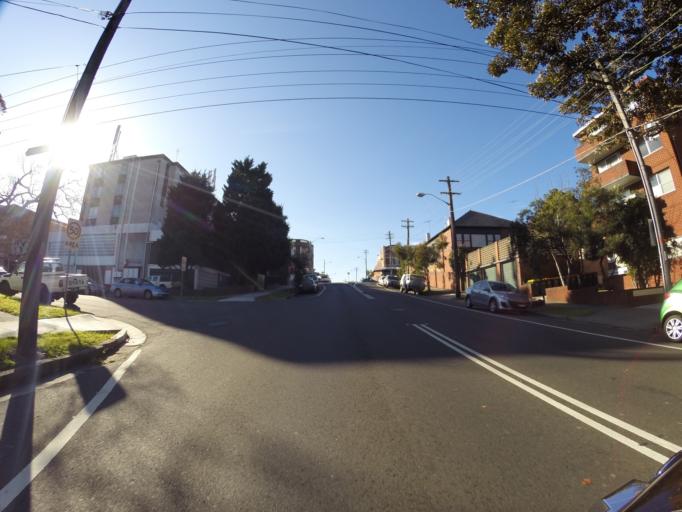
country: AU
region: New South Wales
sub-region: Randwick
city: Clovelly
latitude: -33.9128
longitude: 151.2585
